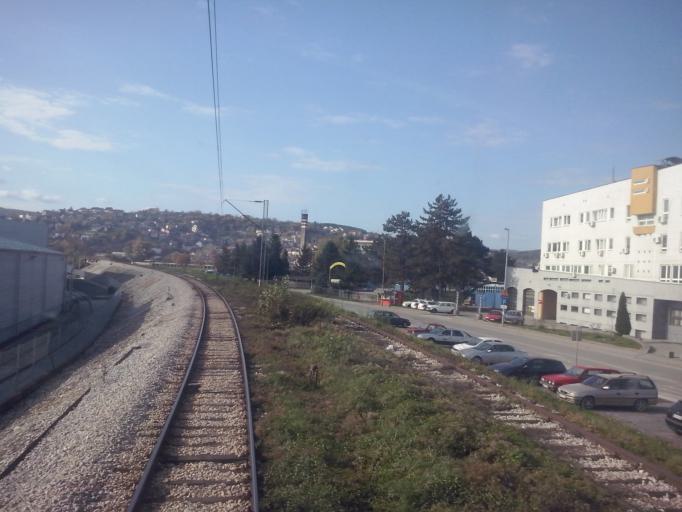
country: RS
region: Central Serbia
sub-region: Kolubarski Okrug
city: Valjevo
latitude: 44.2691
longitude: 19.8988
